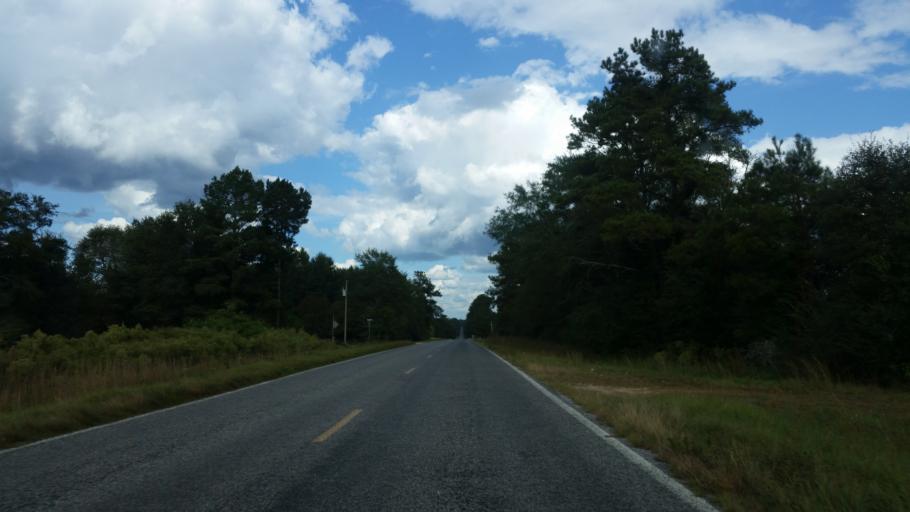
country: US
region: Mississippi
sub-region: Stone County
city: Wiggins
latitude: 30.9128
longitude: -89.0837
